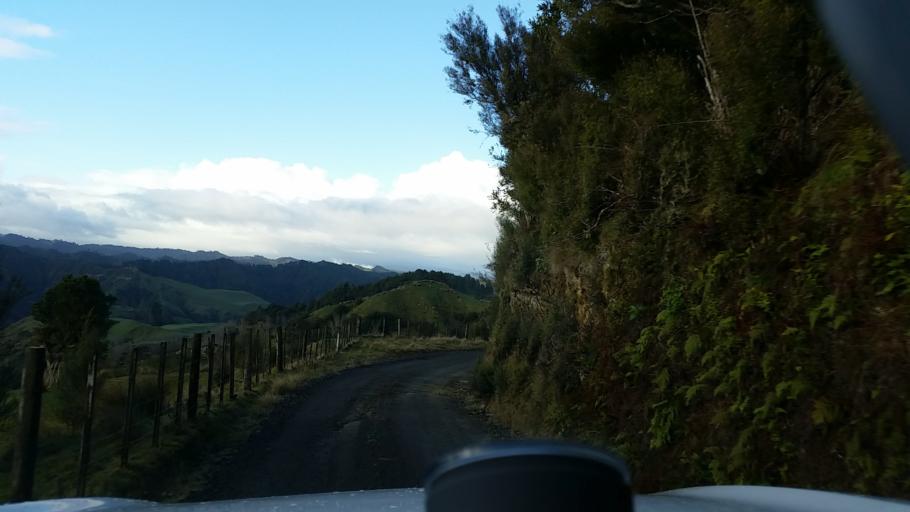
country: NZ
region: Taranaki
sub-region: South Taranaki District
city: Eltham
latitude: -39.4209
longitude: 174.5569
